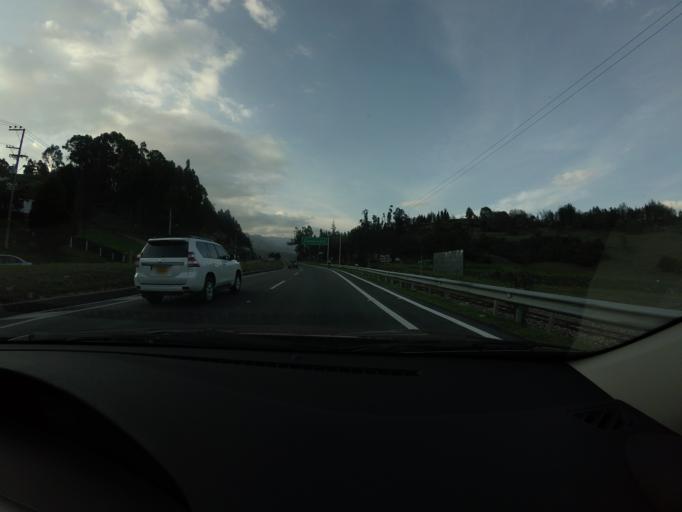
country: CO
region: Cundinamarca
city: Zipaquira
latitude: 4.9978
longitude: -74.0035
